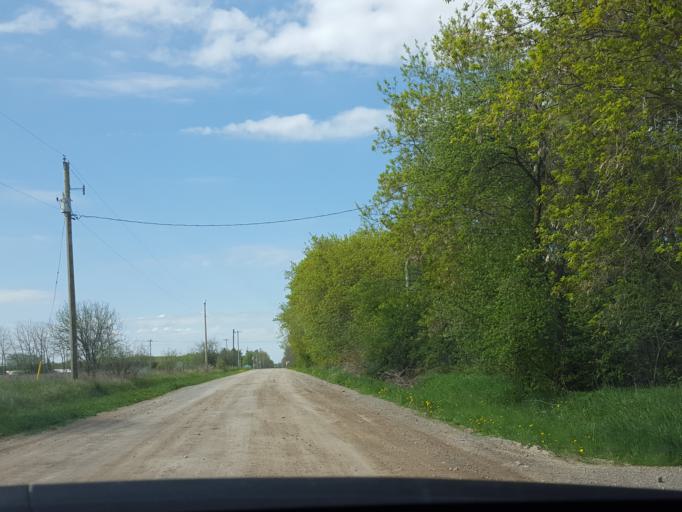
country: CA
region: Ontario
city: Uxbridge
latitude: 44.2036
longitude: -78.8743
